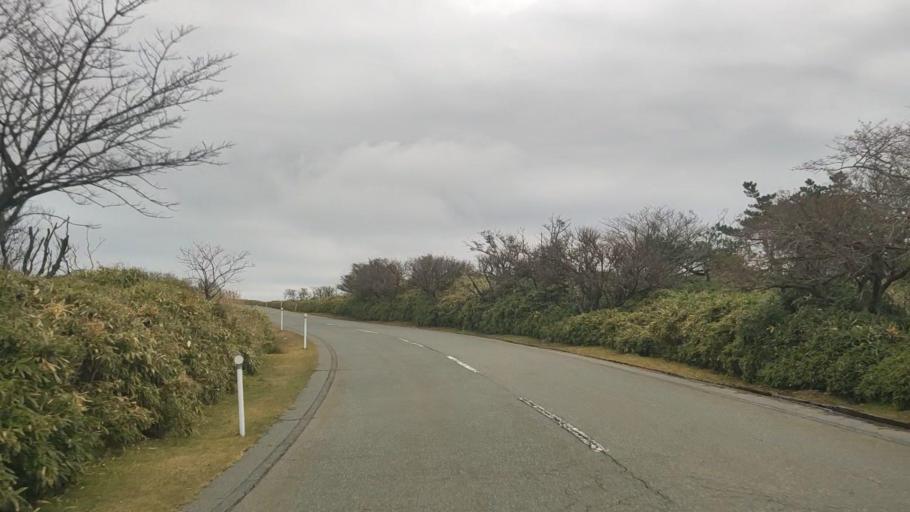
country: JP
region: Shizuoka
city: Heda
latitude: 34.9399
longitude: 138.8365
